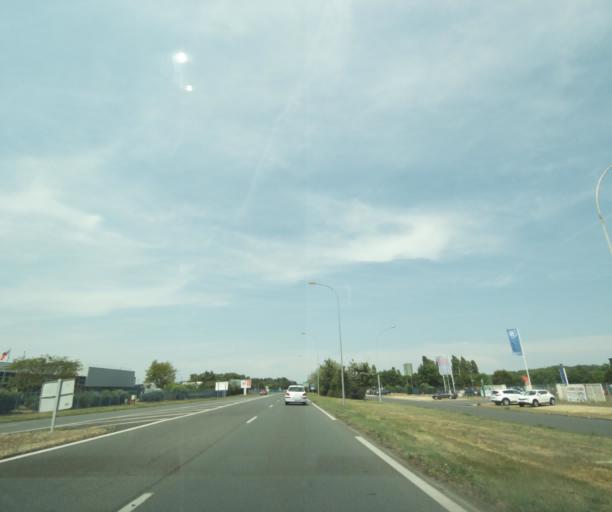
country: FR
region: Poitou-Charentes
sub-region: Departement de la Vienne
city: Antran
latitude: 46.8467
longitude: 0.5502
